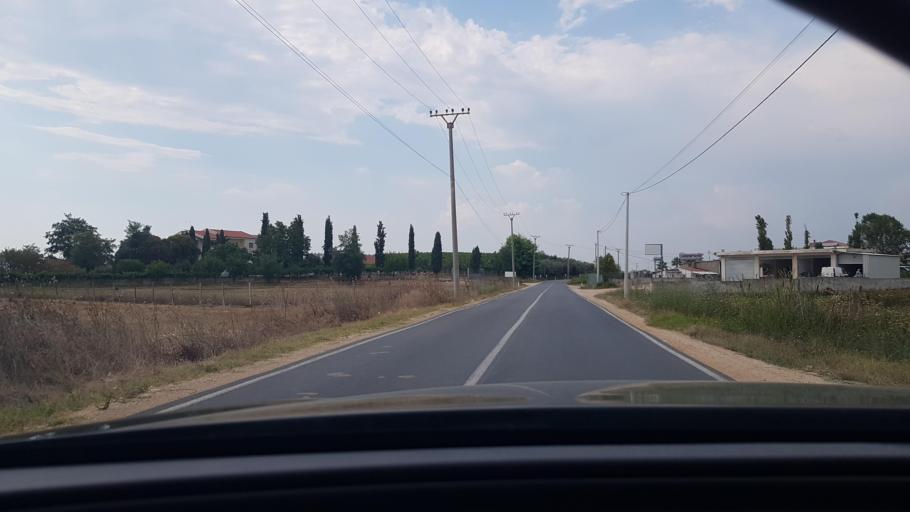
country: AL
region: Durres
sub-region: Rrethi i Durresit
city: Katundi i Ri
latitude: 41.4130
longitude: 19.5467
